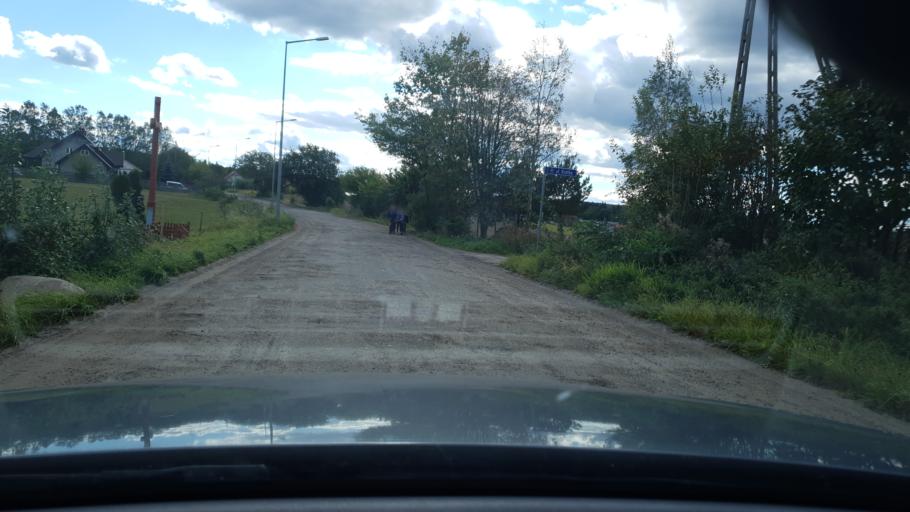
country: PL
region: Pomeranian Voivodeship
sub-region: Powiat wejherowski
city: Reda
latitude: 54.5768
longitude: 18.3102
